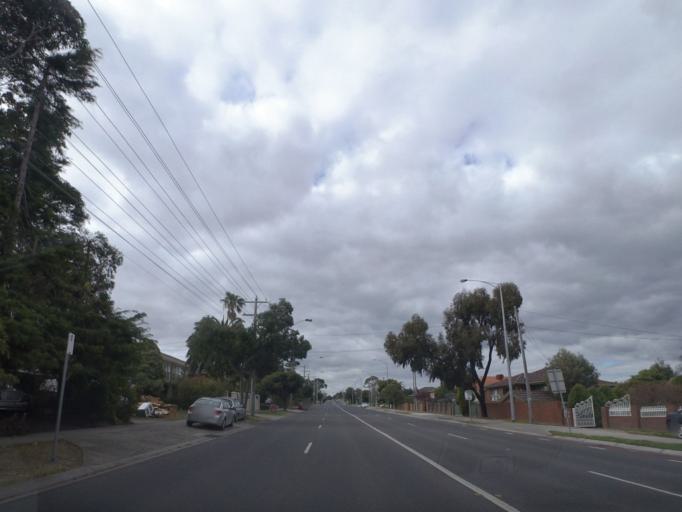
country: AU
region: Victoria
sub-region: Boroondara
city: Balwyn North
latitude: -37.7853
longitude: 145.1066
